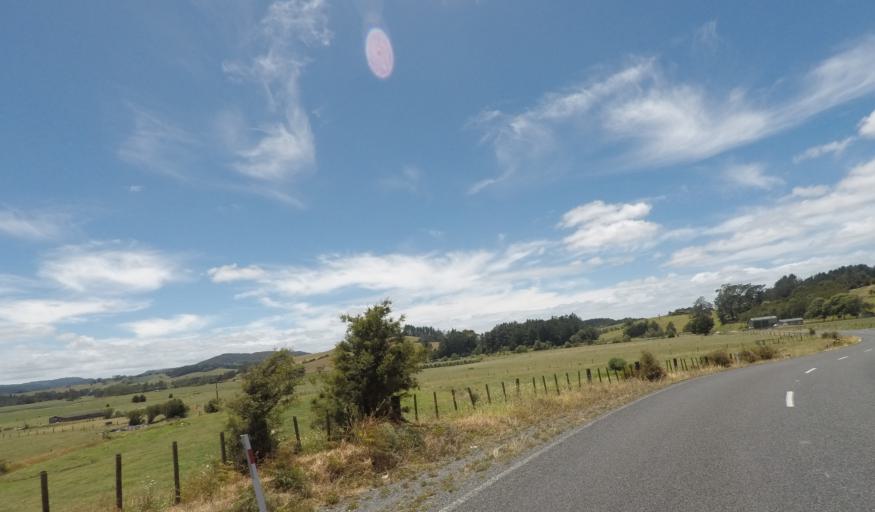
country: NZ
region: Northland
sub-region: Whangarei
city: Whangarei
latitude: -35.5487
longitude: 174.3007
